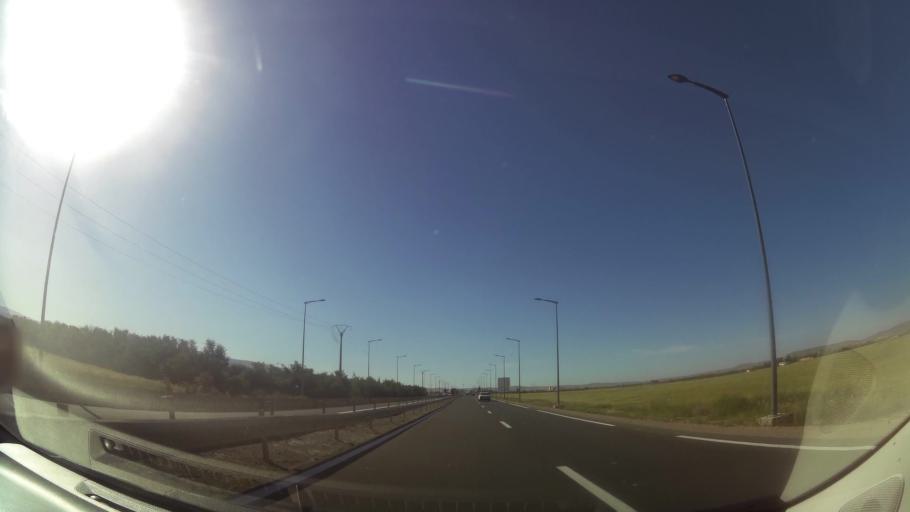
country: MA
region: Oriental
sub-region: Berkane-Taourirt
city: Ahfir
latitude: 34.8371
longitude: -1.9790
